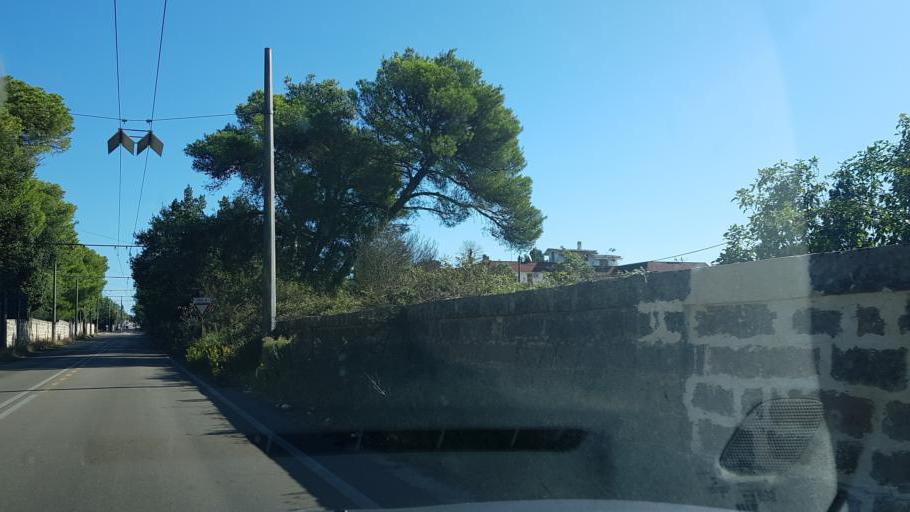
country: IT
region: Apulia
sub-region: Provincia di Lecce
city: San Pietro in Lama
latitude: 40.3388
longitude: 18.1340
